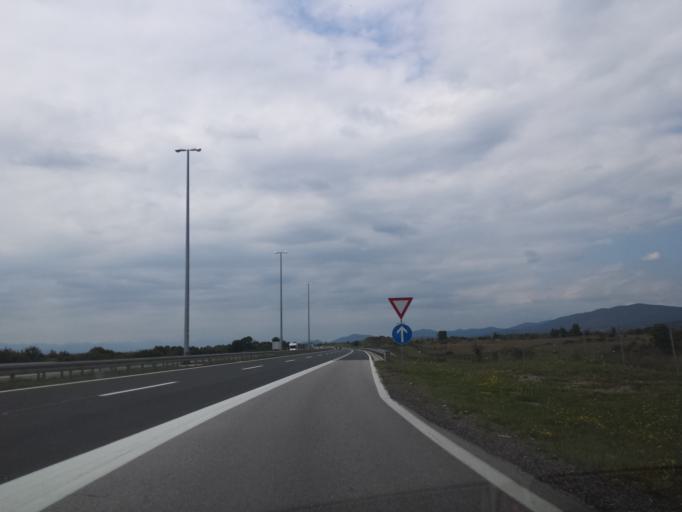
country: HR
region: Zadarska
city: Starigrad
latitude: 44.4638
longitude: 15.6008
